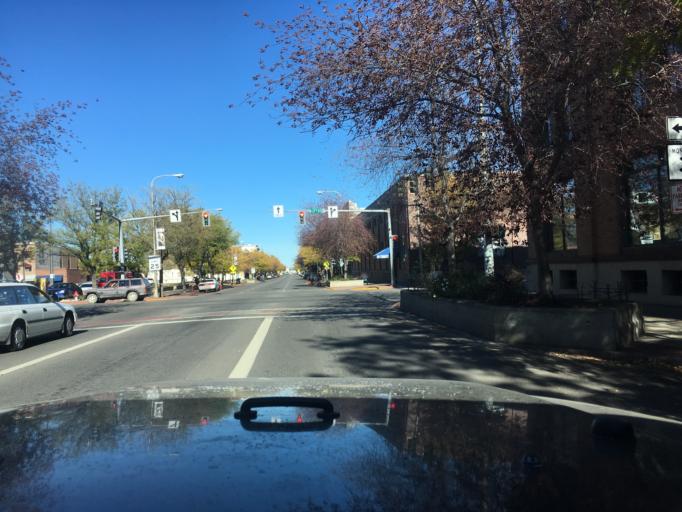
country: US
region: Montana
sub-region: Yellowstone County
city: Billings
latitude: 45.7817
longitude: -108.5041
